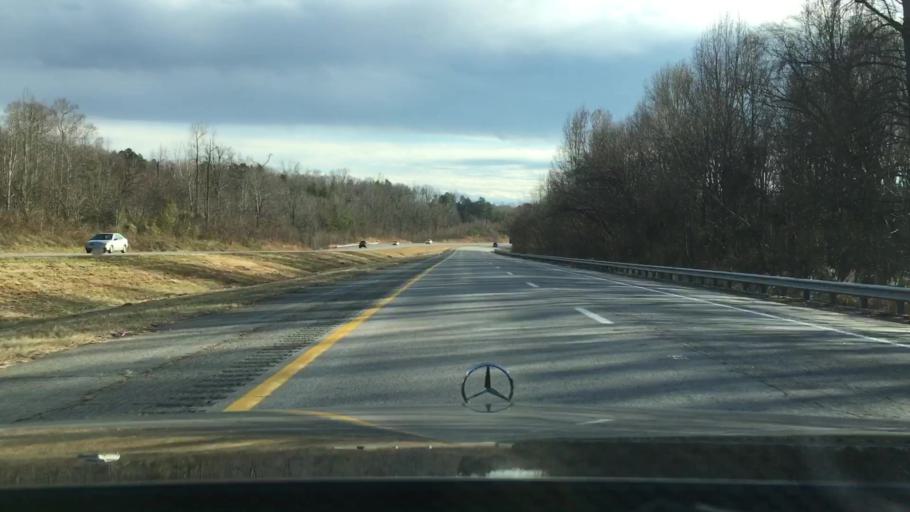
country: US
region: Virginia
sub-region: City of Danville
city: Danville
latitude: 36.6066
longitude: -79.3579
